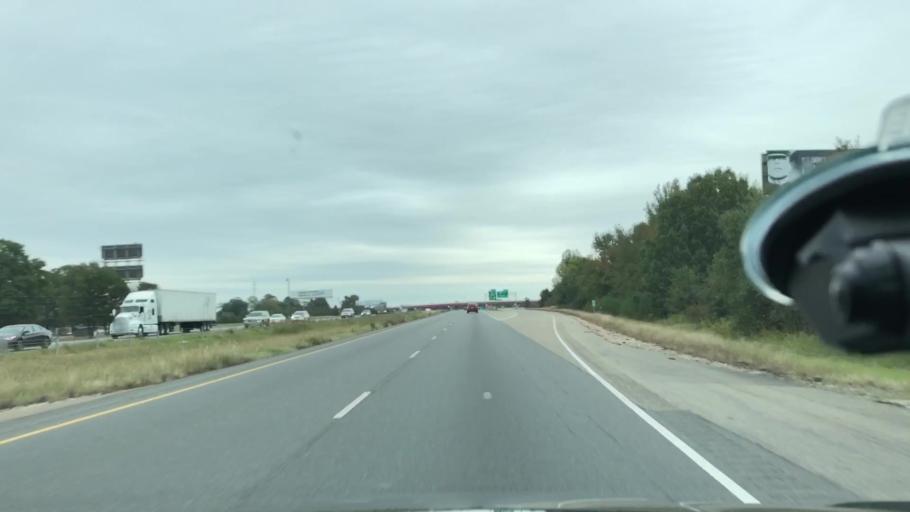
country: US
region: Arkansas
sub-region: Miller County
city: Texarkana
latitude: 33.4778
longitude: -93.9967
